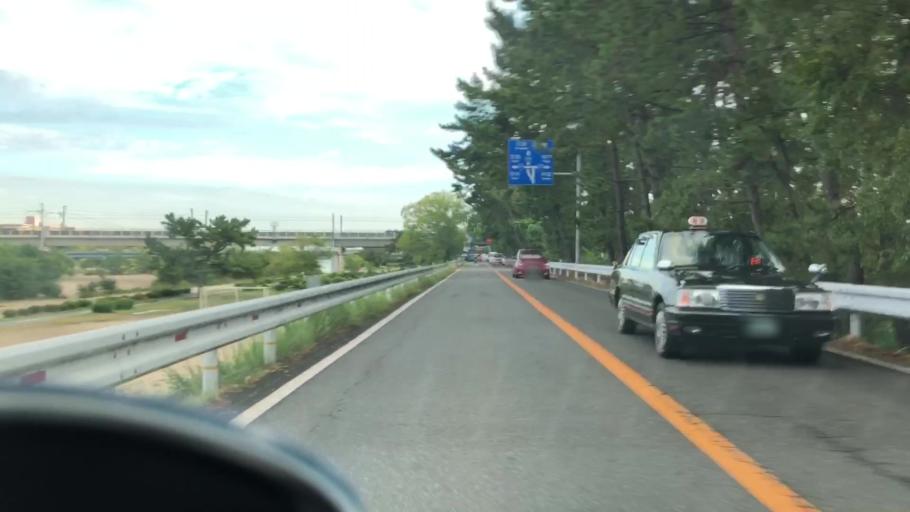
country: JP
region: Hyogo
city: Itami
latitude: 34.7685
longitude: 135.3726
